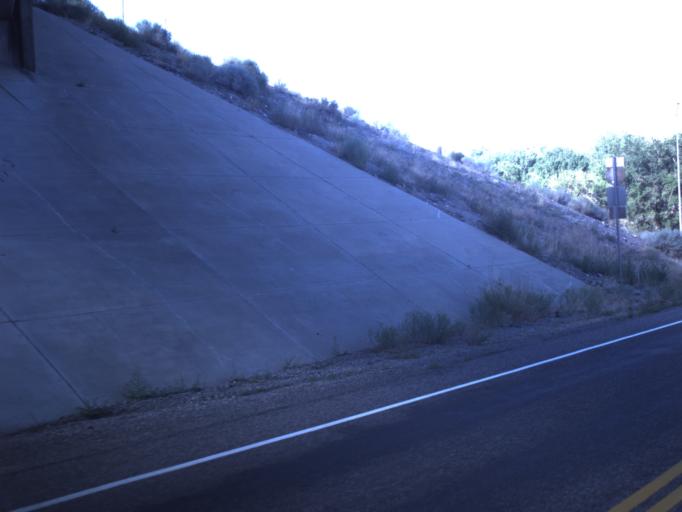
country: US
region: Utah
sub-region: Sevier County
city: Monroe
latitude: 38.6829
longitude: -112.1561
